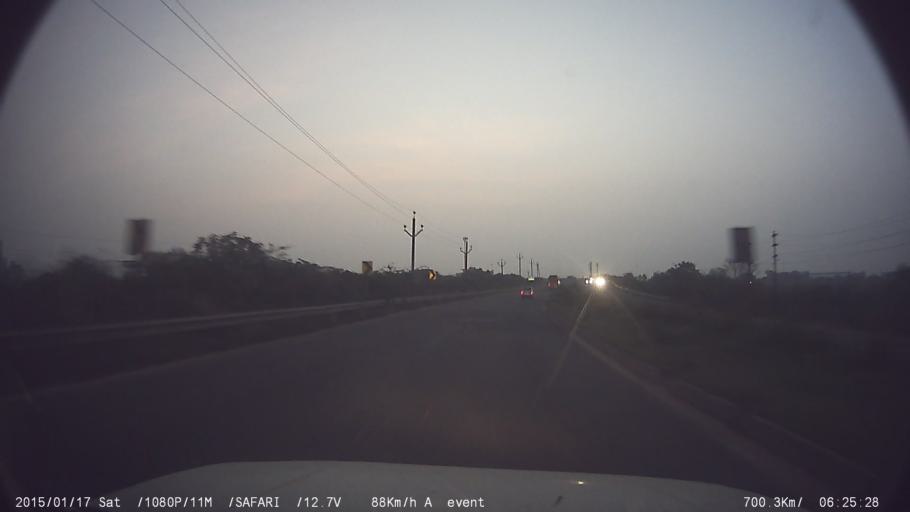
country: IN
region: Tamil Nadu
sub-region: Kancheepuram
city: Sriperumbudur
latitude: 12.9225
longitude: 79.8761
